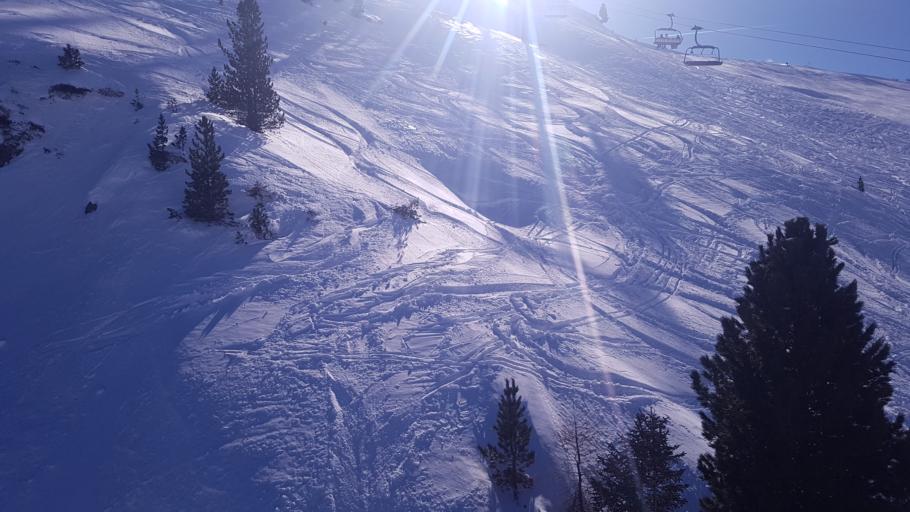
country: AT
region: Salzburg
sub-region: Politischer Bezirk Zell am See
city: Neukirchen am Grossvenediger
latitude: 47.2881
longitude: 12.2865
